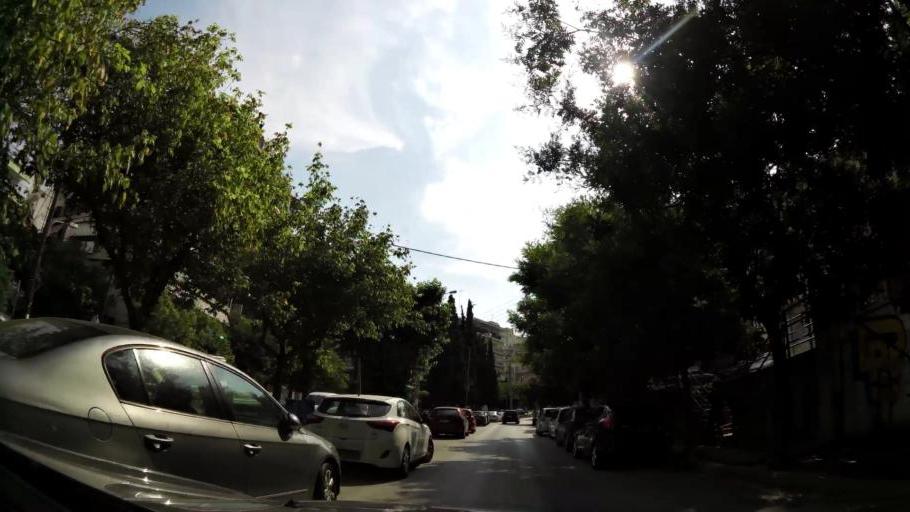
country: GR
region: Central Macedonia
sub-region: Nomos Thessalonikis
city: Sykies
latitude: 40.6513
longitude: 22.9519
